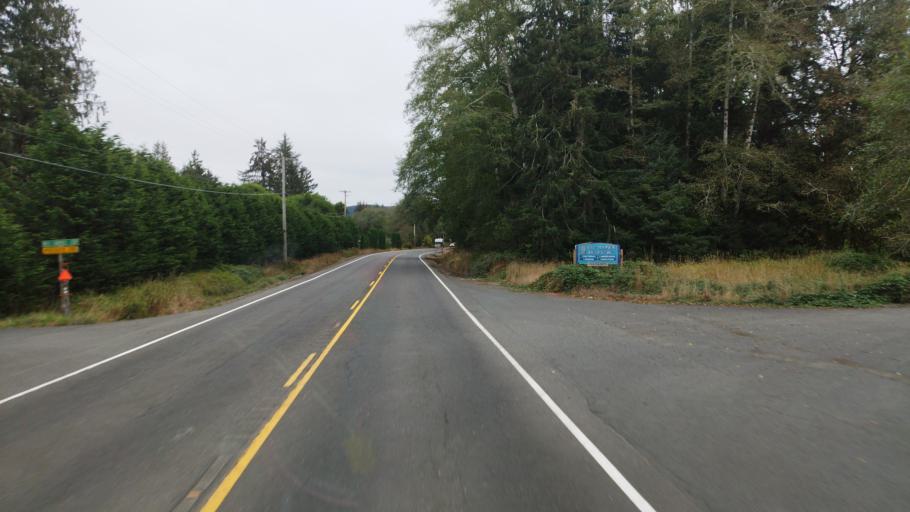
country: US
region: Oregon
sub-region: Clatsop County
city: Cannon Beach
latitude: 45.9141
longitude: -123.8885
